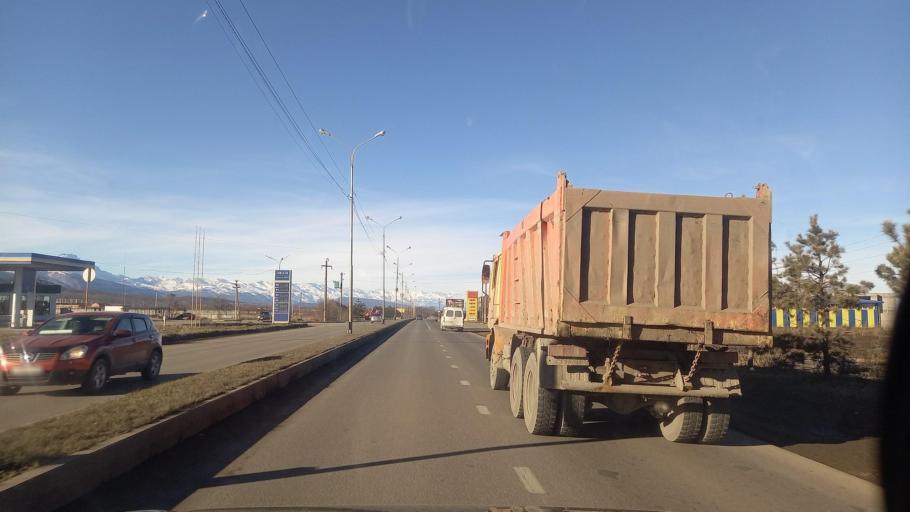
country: RU
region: North Ossetia
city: Vladikavkaz
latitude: 43.0254
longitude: 44.6345
